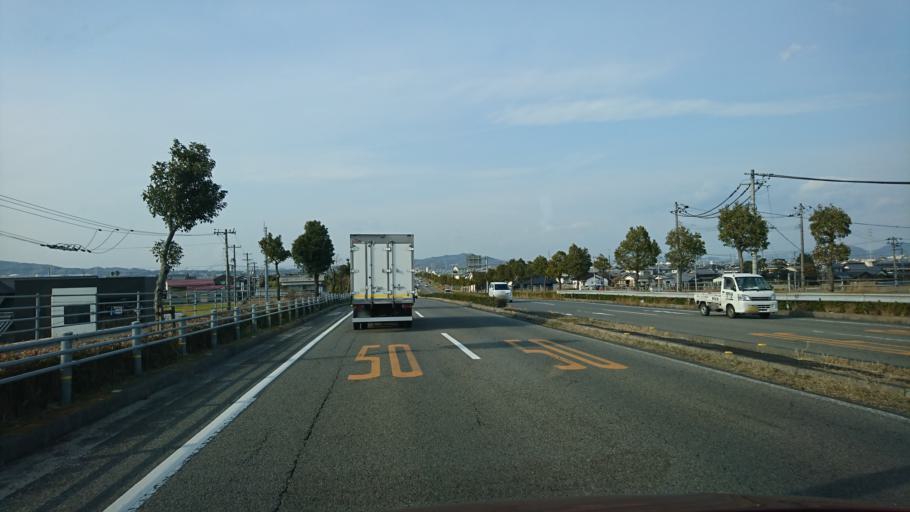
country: JP
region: Ehime
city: Saijo
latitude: 34.0231
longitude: 133.0102
